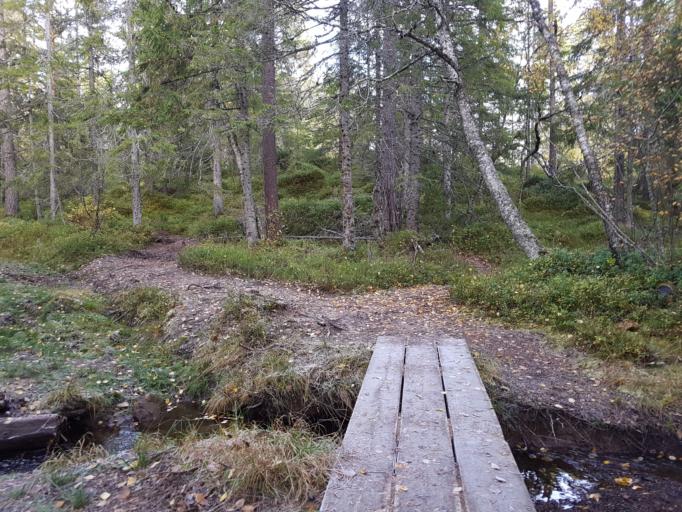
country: NO
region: Sor-Trondelag
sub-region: Trondheim
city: Trondheim
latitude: 63.4473
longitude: 10.2740
